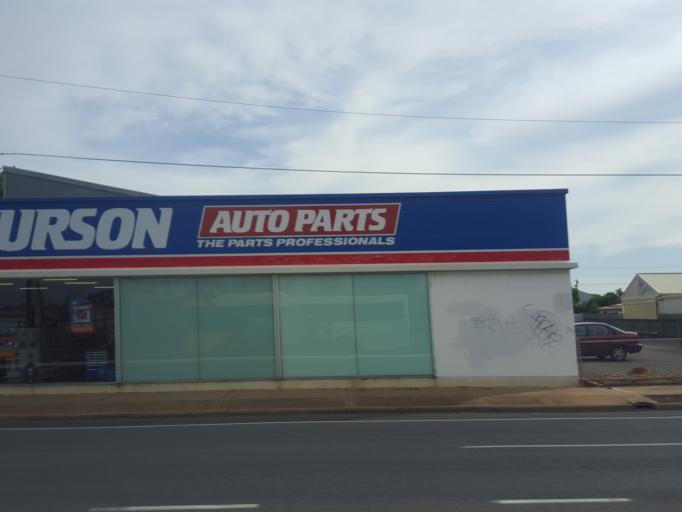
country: AU
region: South Australia
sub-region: Charles Sturt
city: Woodville
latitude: -34.8792
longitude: 138.5550
